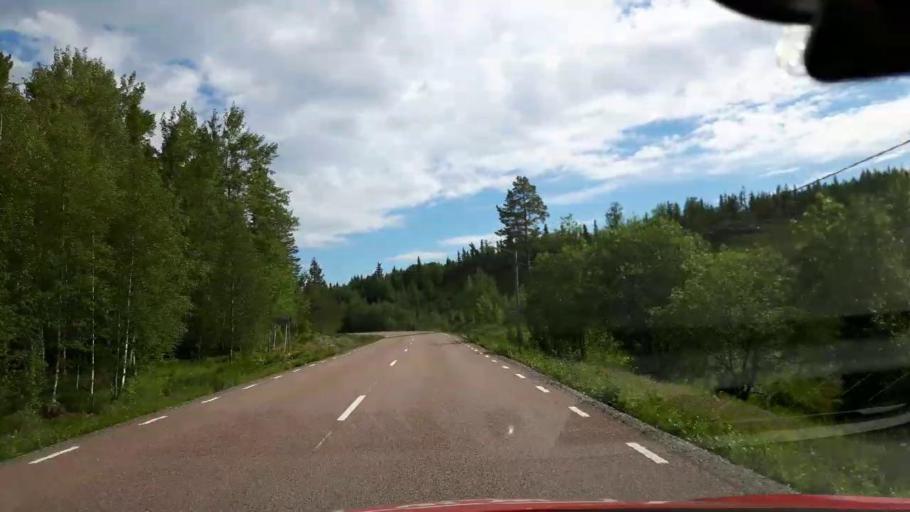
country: SE
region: Jaemtland
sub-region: Krokoms Kommun
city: Valla
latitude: 63.9290
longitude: 14.2109
